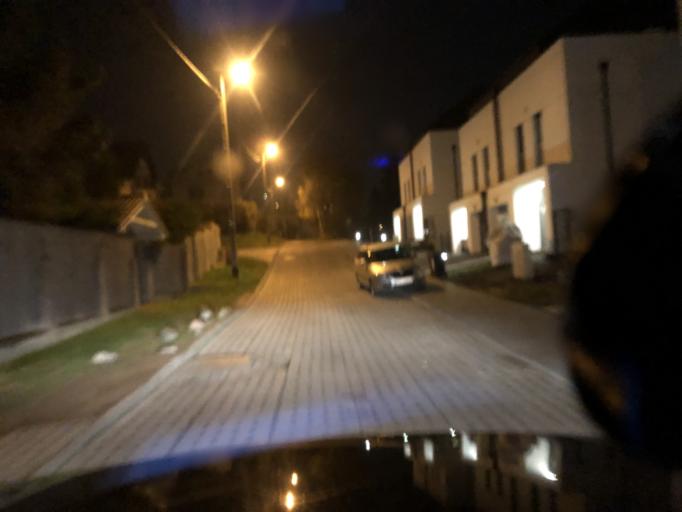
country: PL
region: Pomeranian Voivodeship
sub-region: Powiat gdanski
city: Kowale
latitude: 54.3432
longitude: 18.5770
